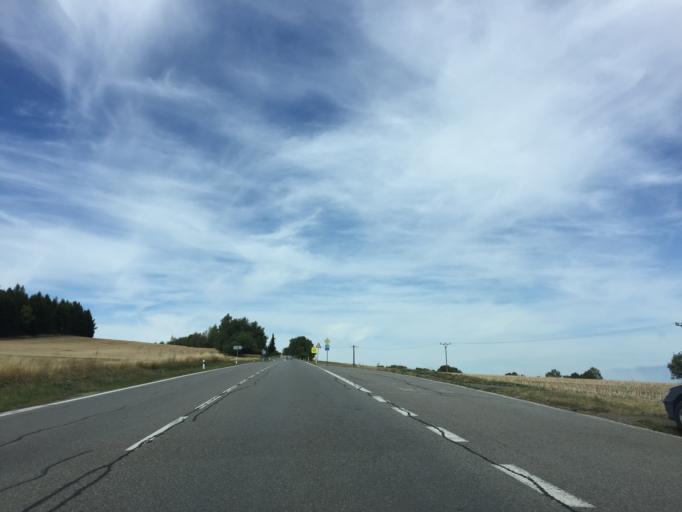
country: CZ
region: Jihocesky
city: Chotoviny
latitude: 49.5520
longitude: 14.6659
